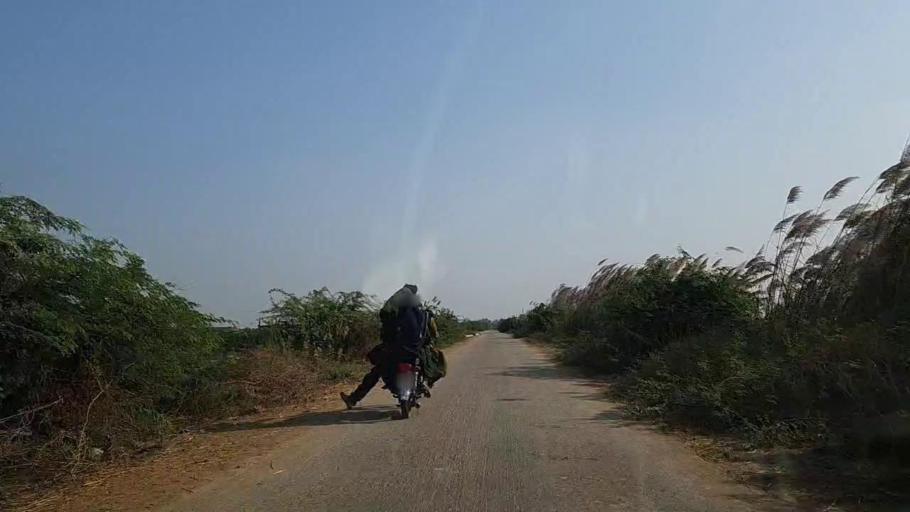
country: PK
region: Sindh
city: Mirpur Sakro
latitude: 24.6233
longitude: 67.6567
